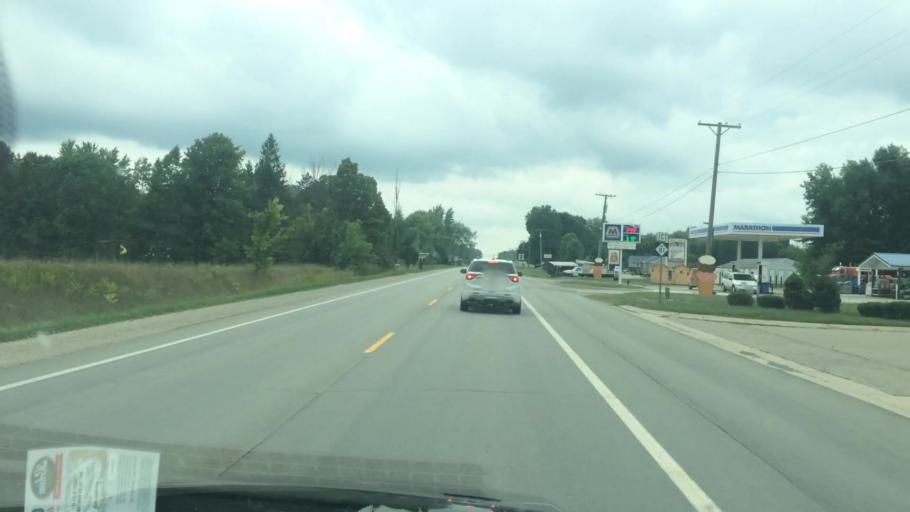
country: US
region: Michigan
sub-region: Tuscola County
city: Cass City
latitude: 43.5985
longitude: -83.0967
